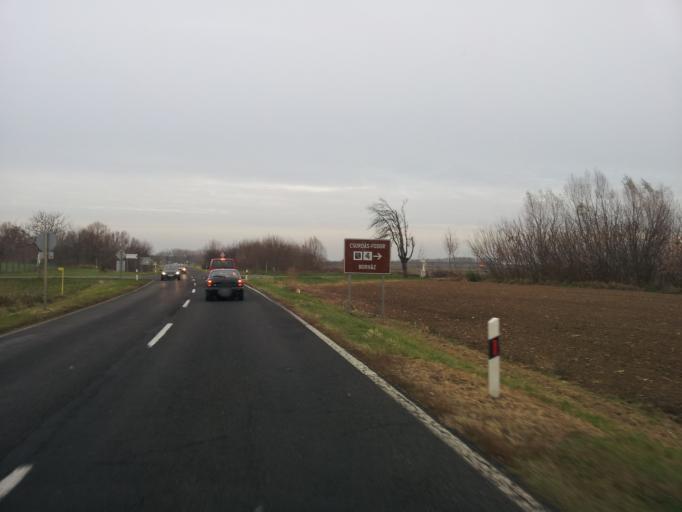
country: HU
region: Veszprem
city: Devecser
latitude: 47.1249
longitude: 17.3762
